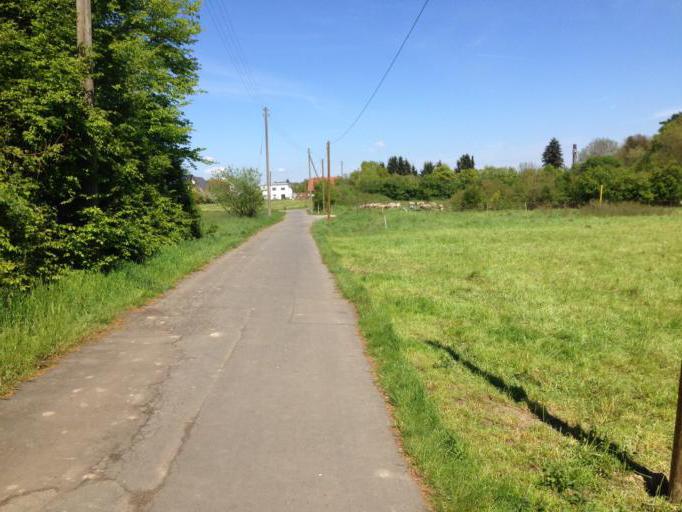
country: DE
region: Hesse
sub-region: Regierungsbezirk Giessen
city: Giessen
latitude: 50.5645
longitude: 8.6669
